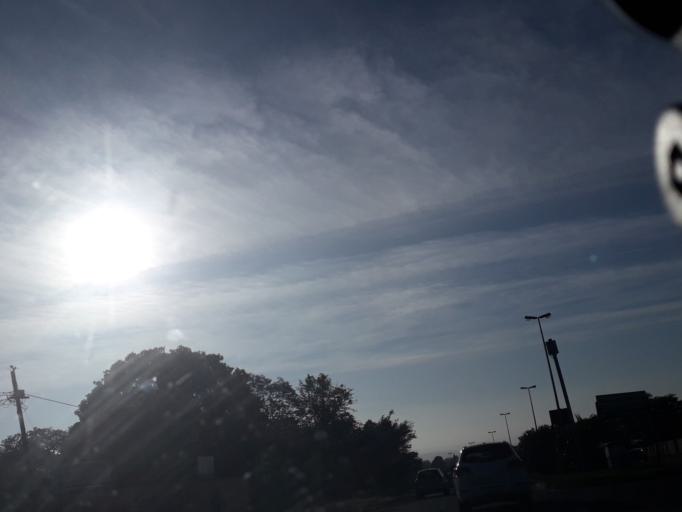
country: ZA
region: Gauteng
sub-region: City of Johannesburg Metropolitan Municipality
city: Roodepoort
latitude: -26.1054
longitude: 27.9267
